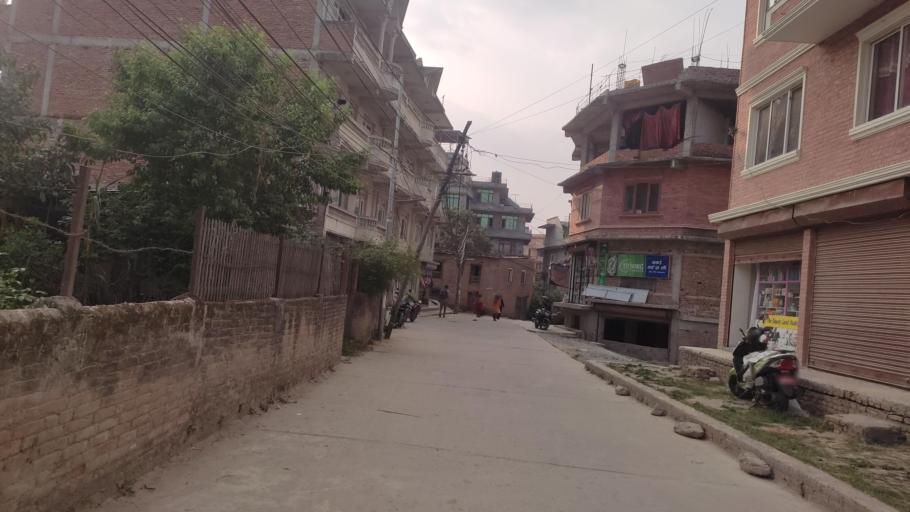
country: NP
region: Central Region
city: Kirtipur
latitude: 27.6732
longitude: 85.2773
